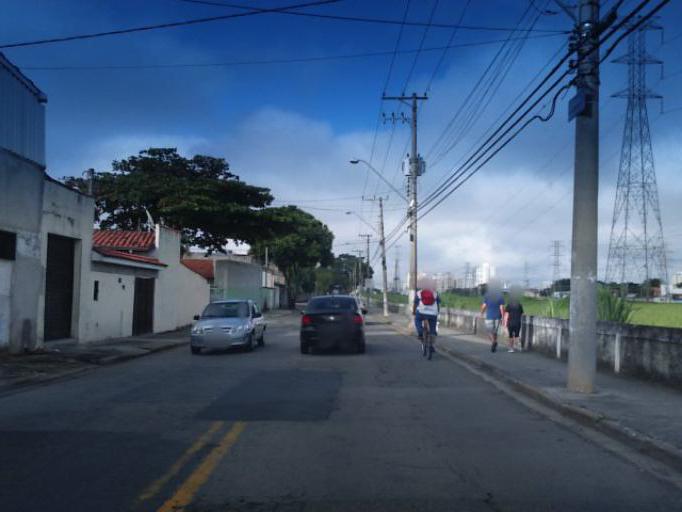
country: BR
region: Sao Paulo
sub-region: Sao Jose Dos Campos
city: Sao Jose dos Campos
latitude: -23.1922
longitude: -45.8712
